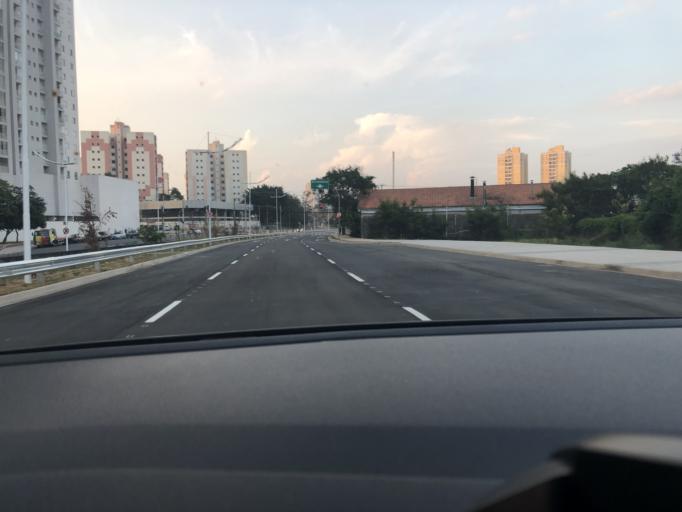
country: BR
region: Sao Paulo
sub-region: Jundiai
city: Jundiai
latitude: -23.1810
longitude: -46.9053
